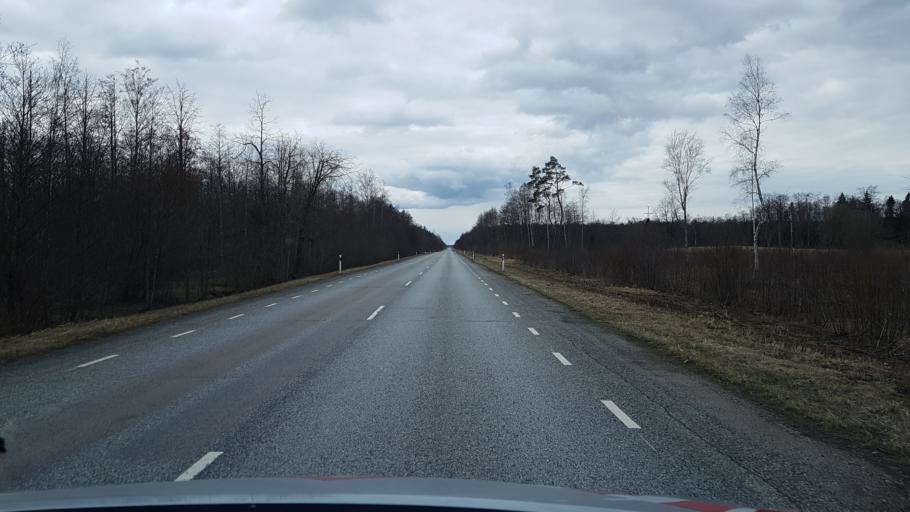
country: EE
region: Ida-Virumaa
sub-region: Narva-Joesuu linn
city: Narva-Joesuu
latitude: 59.3437
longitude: 27.9976
